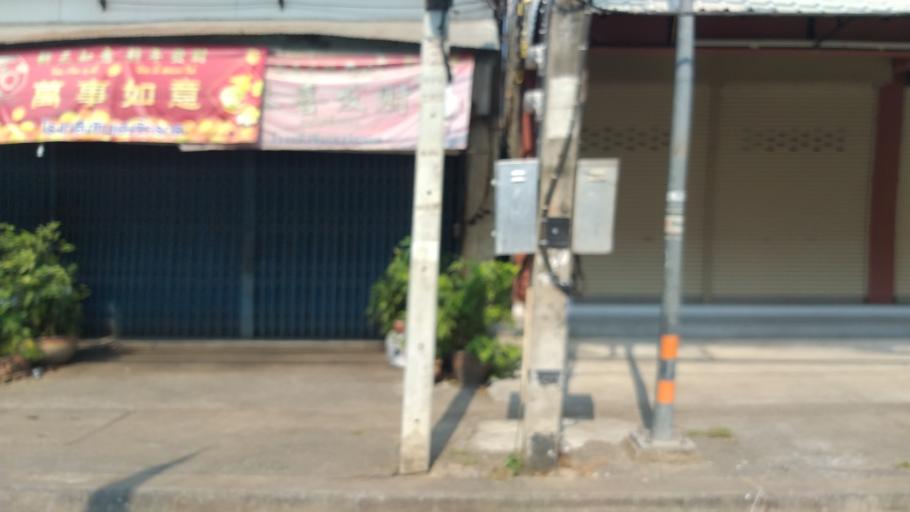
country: TH
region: Changwat Udon Thani
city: Udon Thani
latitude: 17.4019
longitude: 102.7986
